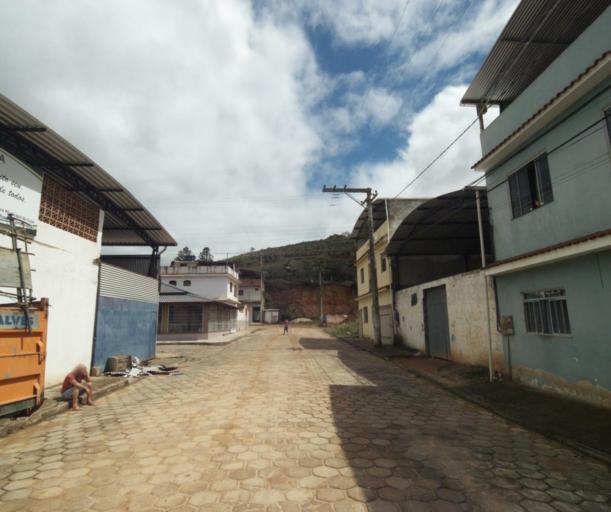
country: BR
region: Espirito Santo
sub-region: Irupi
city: Irupi
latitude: -20.3480
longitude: -41.6469
